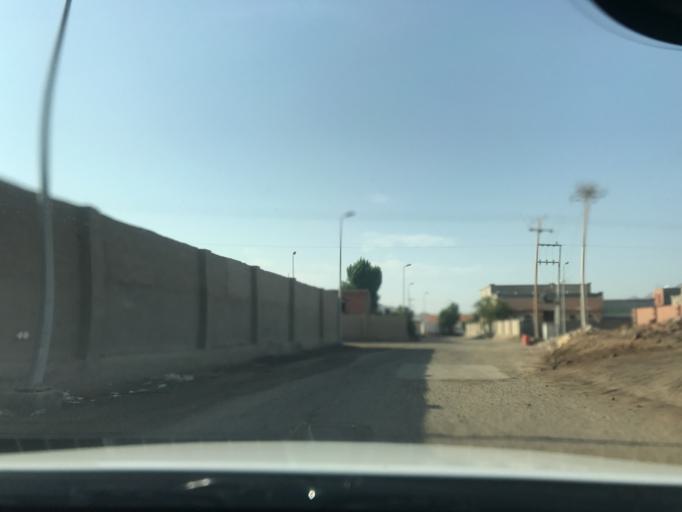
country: SA
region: Makkah
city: Al Jumum
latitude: 21.4490
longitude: 39.5346
